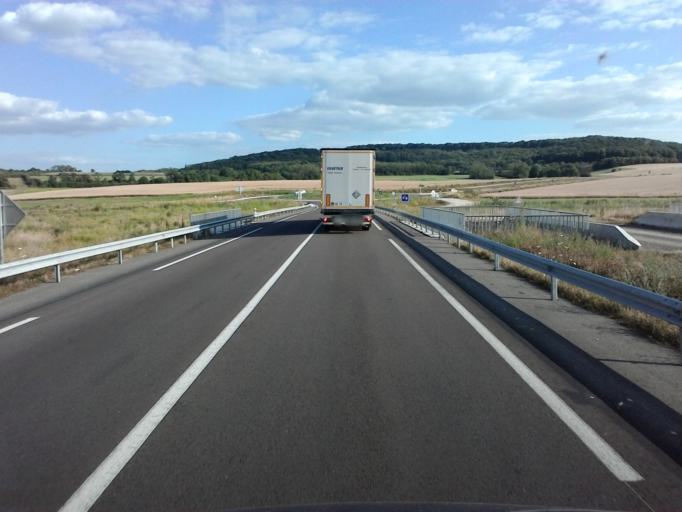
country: FR
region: Franche-Comte
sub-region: Departement de la Haute-Saone
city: Frotey-les-Vesoul
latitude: 47.6884
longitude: 6.2662
